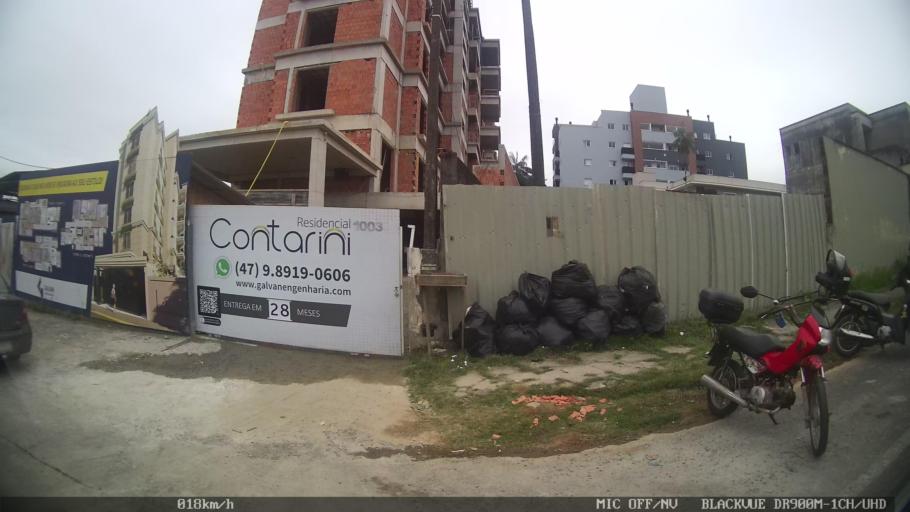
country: BR
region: Santa Catarina
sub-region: Joinville
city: Joinville
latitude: -26.2735
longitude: -48.8436
